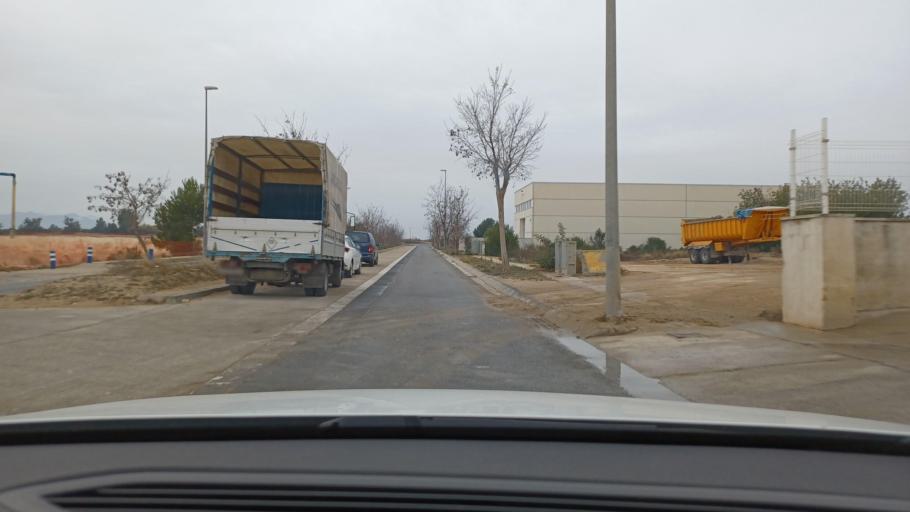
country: ES
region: Catalonia
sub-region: Provincia de Tarragona
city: Amposta
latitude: 40.7648
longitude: 0.5918
